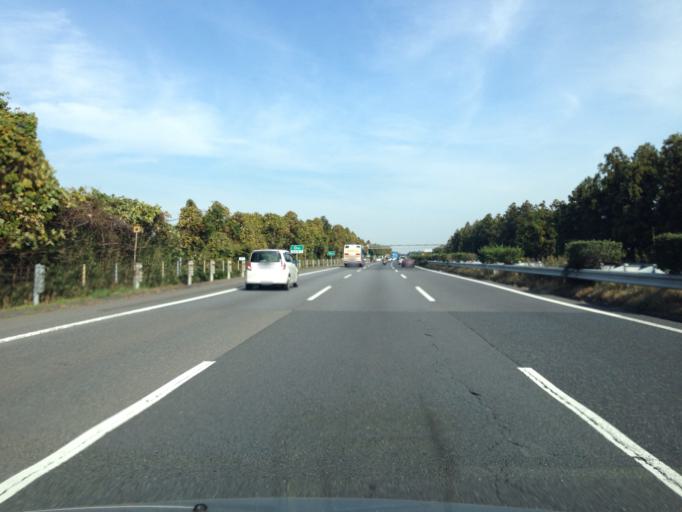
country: JP
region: Ibaraki
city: Naka
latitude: 36.1319
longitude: 140.1955
